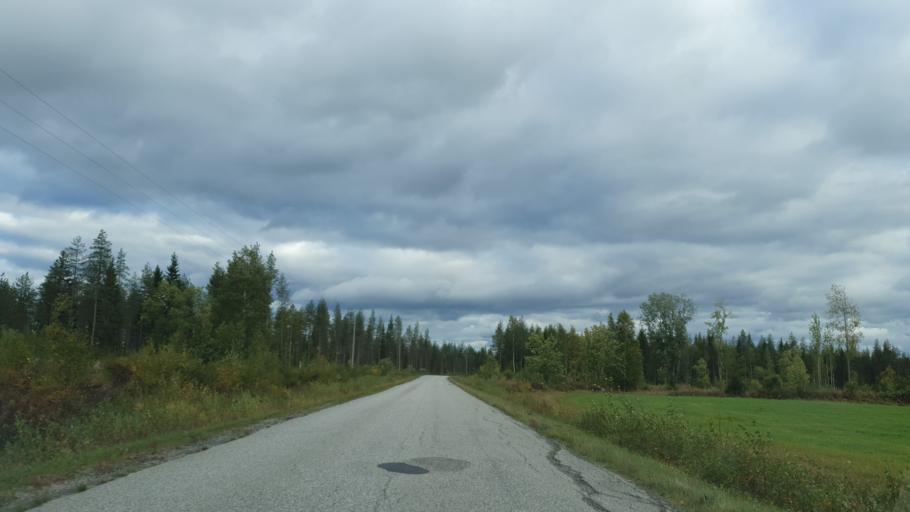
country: FI
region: Kainuu
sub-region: Kehys-Kainuu
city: Kuhmo
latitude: 63.9516
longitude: 29.8018
